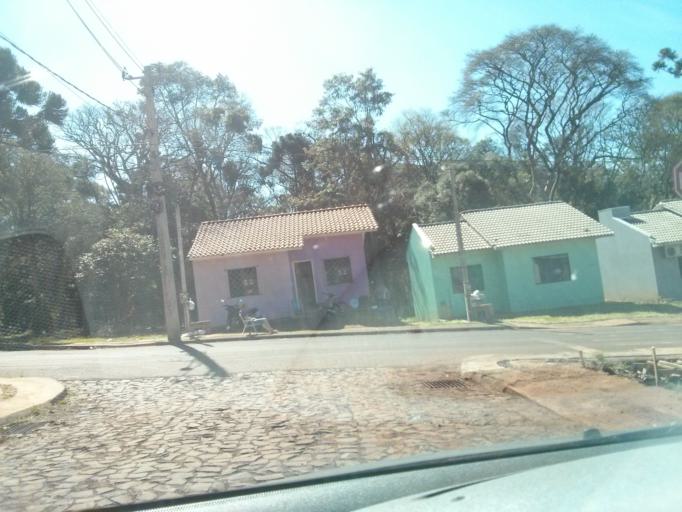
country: BR
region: Santa Catarina
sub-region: Chapeco
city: Chapeco
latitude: -27.0890
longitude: -52.6894
